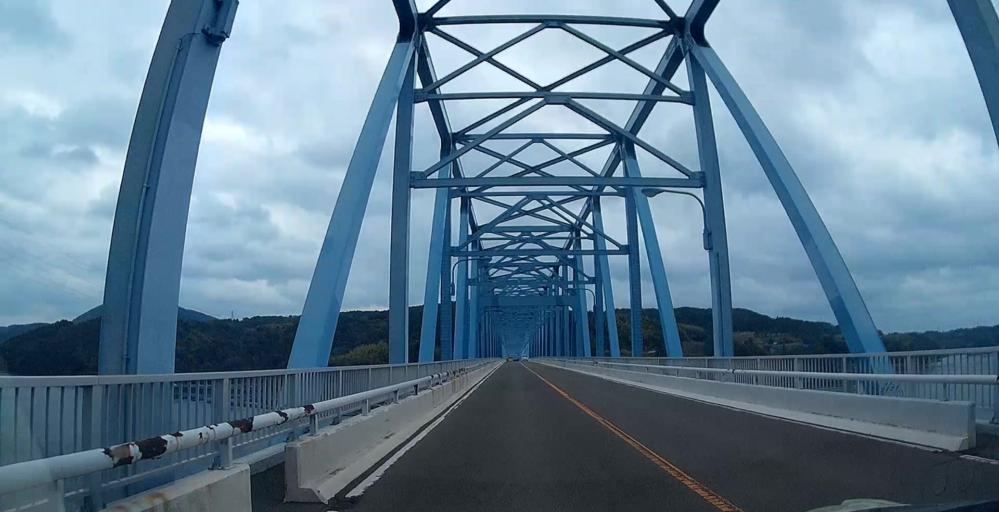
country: JP
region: Kagoshima
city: Akune
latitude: 32.1068
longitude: 130.1727
